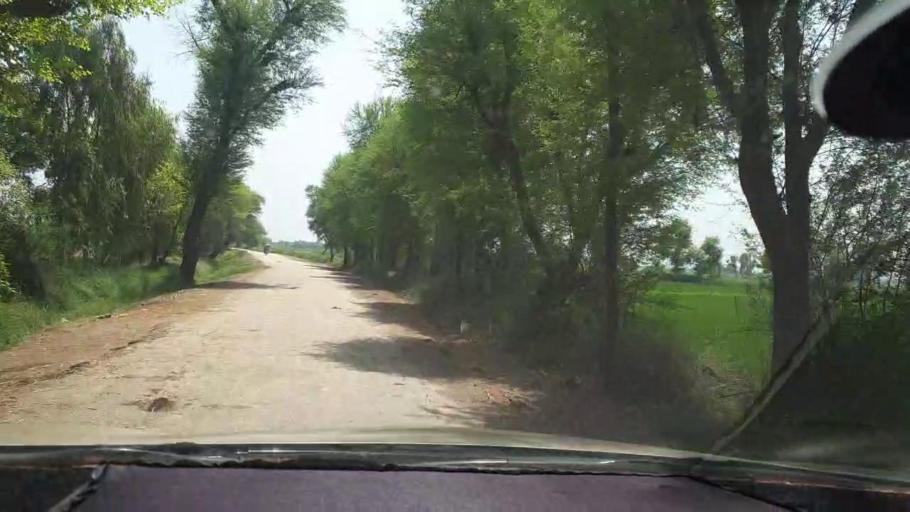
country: PK
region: Sindh
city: Kambar
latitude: 27.6842
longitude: 67.9378
